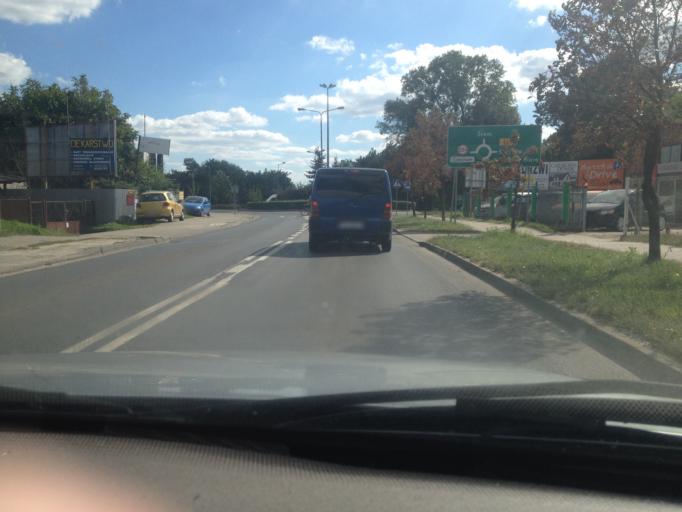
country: PL
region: Greater Poland Voivodeship
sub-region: Powiat poznanski
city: Mosina
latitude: 52.2460
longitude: 16.8470
